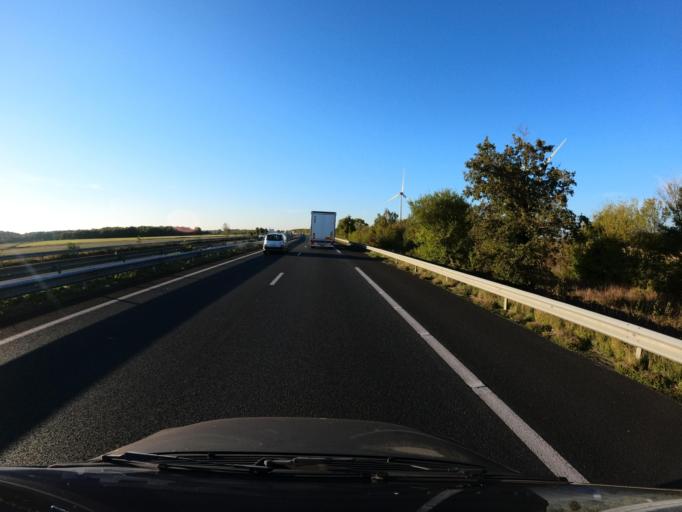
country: FR
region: Pays de la Loire
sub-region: Departement de la Vendee
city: Chauche
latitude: 46.8342
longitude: -1.2281
